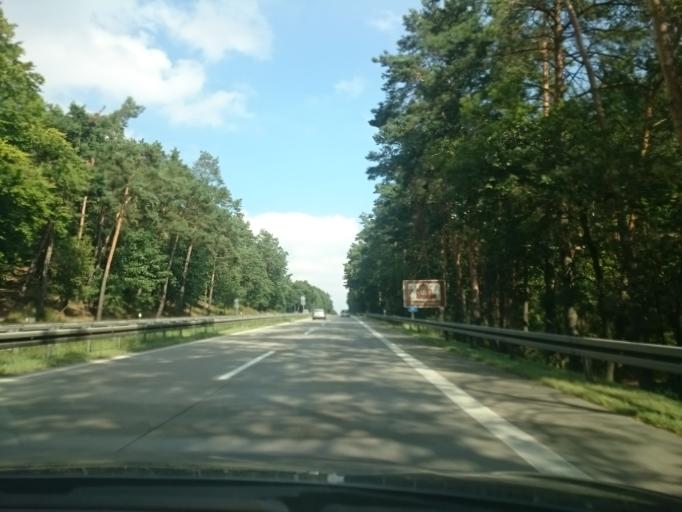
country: DE
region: Brandenburg
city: Britz
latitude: 52.9064
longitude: 13.7440
